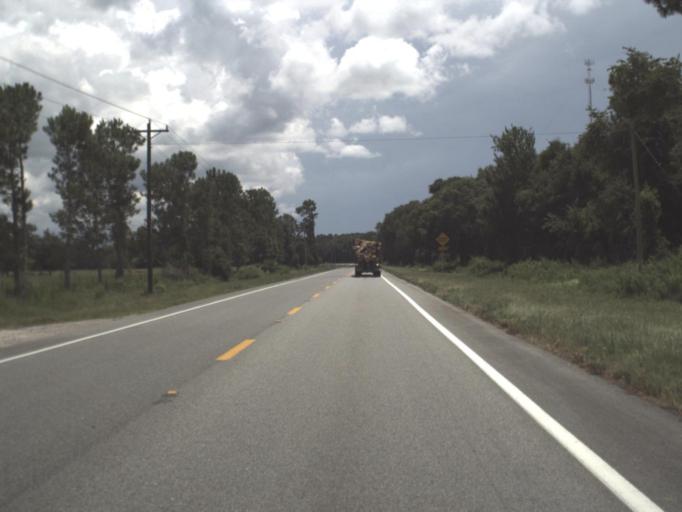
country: US
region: Florida
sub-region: Taylor County
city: Perry
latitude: 30.0875
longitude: -83.6726
